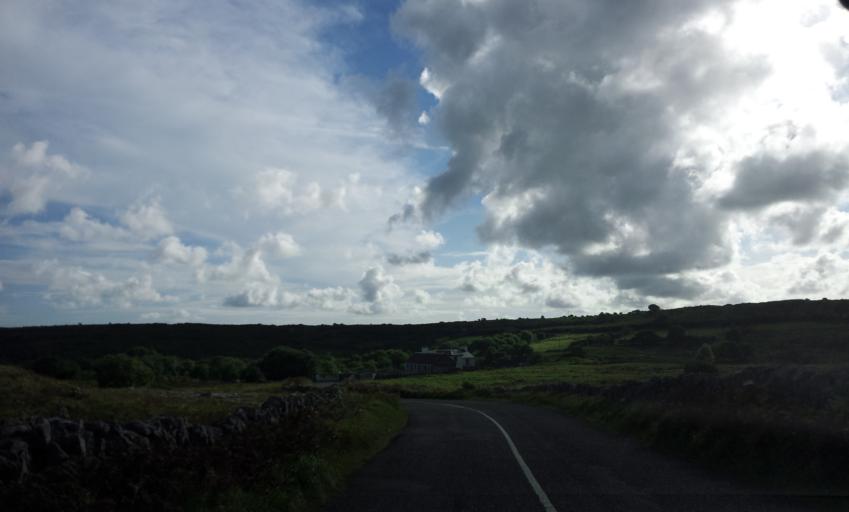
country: IE
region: Connaught
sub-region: County Galway
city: Bearna
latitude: 53.0560
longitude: -9.1465
